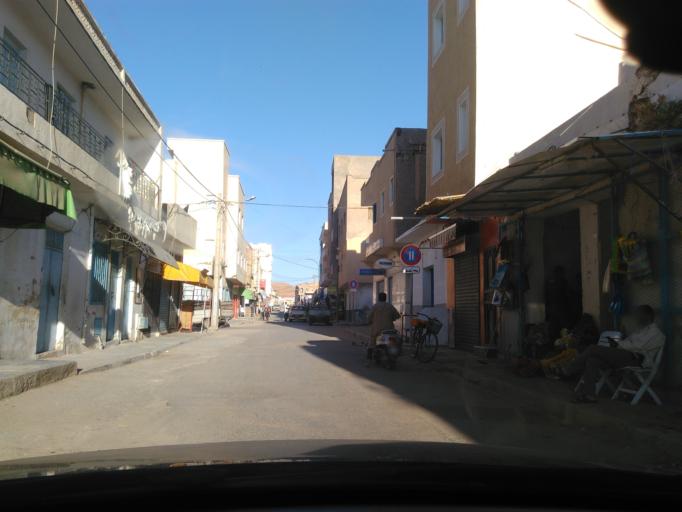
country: TN
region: Tataouine
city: Tataouine
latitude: 32.9284
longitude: 10.4499
